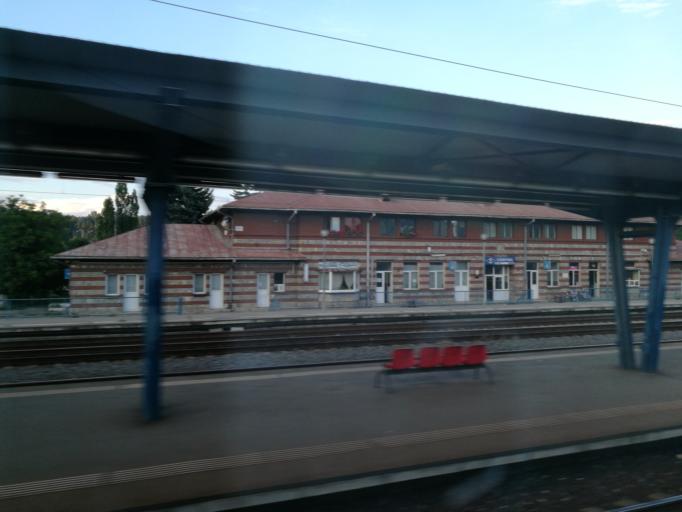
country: RO
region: Prahova
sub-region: Municipiul Campina
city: Campina
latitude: 45.1322
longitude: 25.7111
